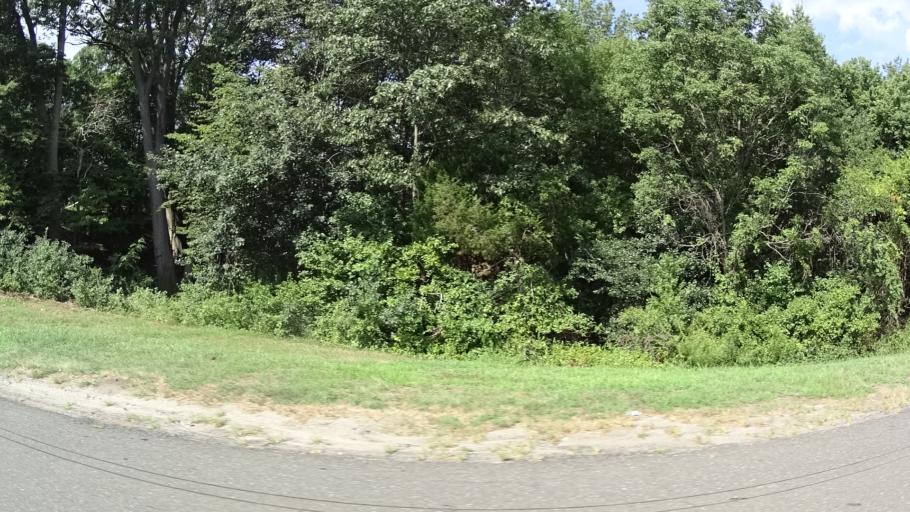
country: US
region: New Jersey
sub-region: Monmouth County
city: Tinton Falls
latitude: 40.3224
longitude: -74.0989
